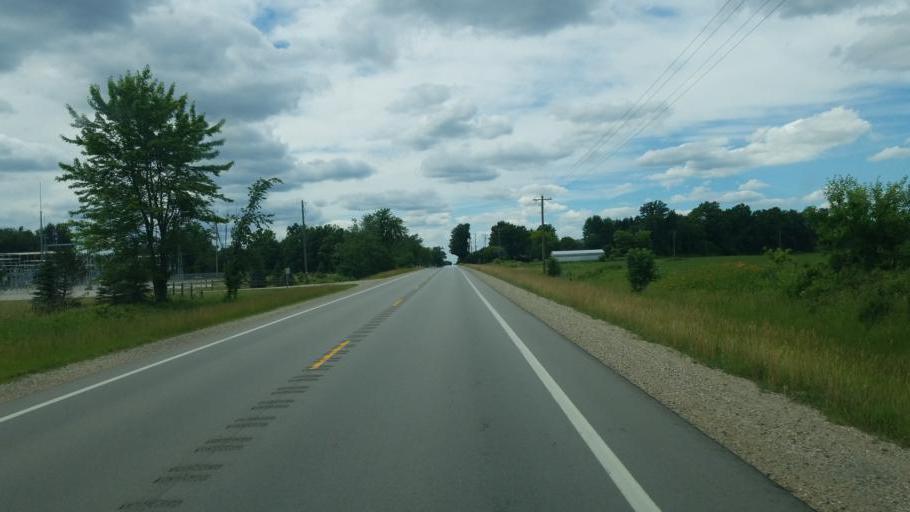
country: US
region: Michigan
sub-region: Eaton County
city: Charlotte
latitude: 42.6501
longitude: -84.8986
